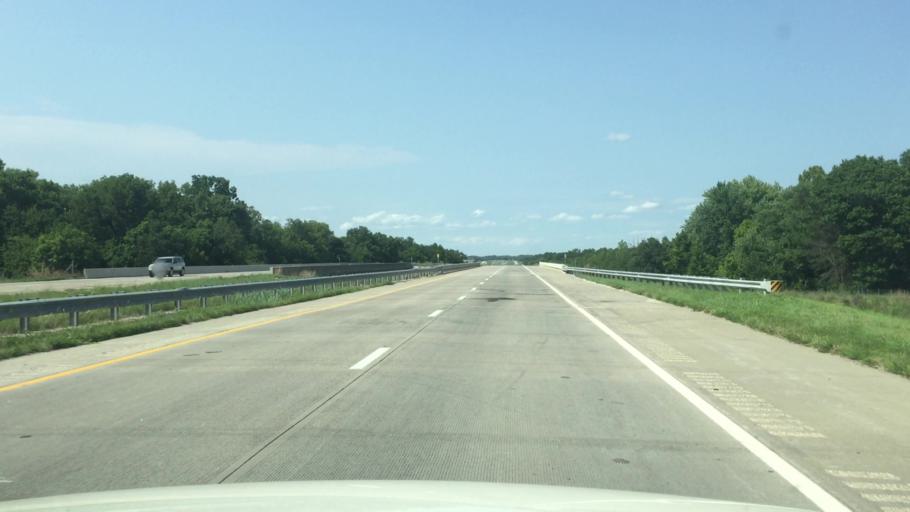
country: US
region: Kansas
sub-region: Linn County
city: La Cygne
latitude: 38.2986
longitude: -94.6773
